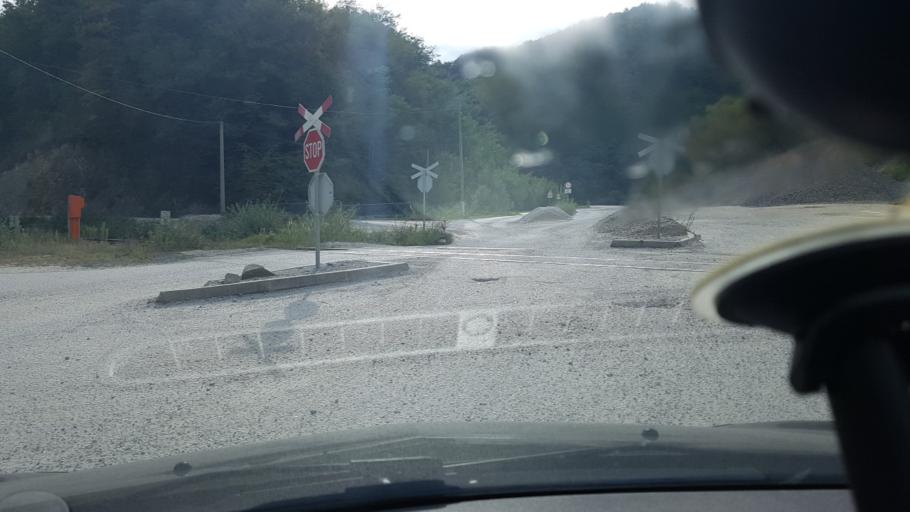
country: HR
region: Krapinsko-Zagorska
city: Mihovljan
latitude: 46.1856
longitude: 15.9843
